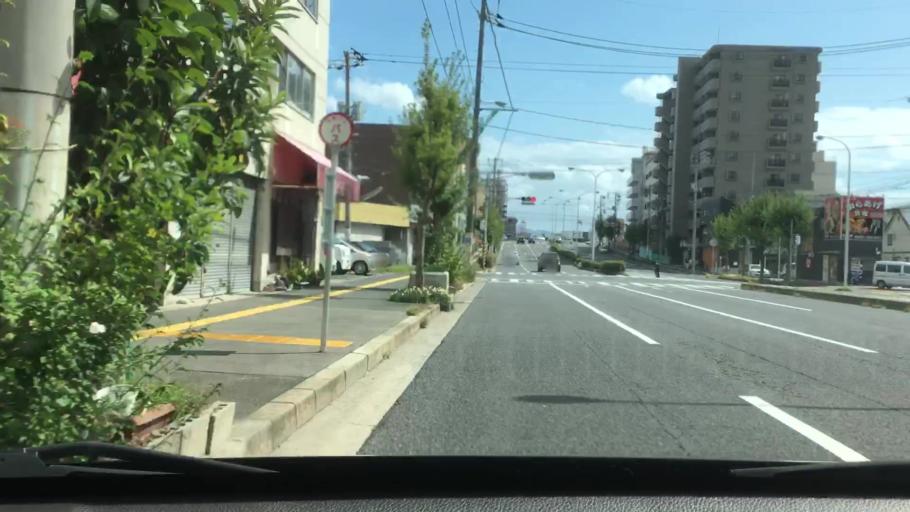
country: JP
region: Hiroshima
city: Hiroshima-shi
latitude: 34.3750
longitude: 132.4388
